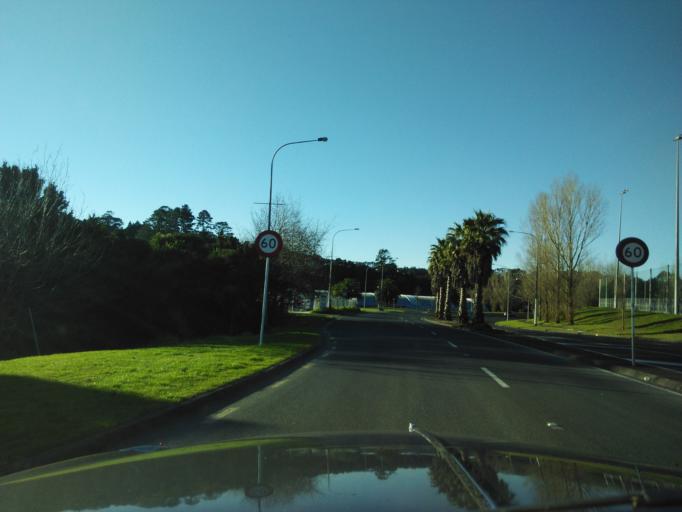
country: NZ
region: Auckland
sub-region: Auckland
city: Rothesay Bay
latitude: -36.7267
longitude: 174.6983
